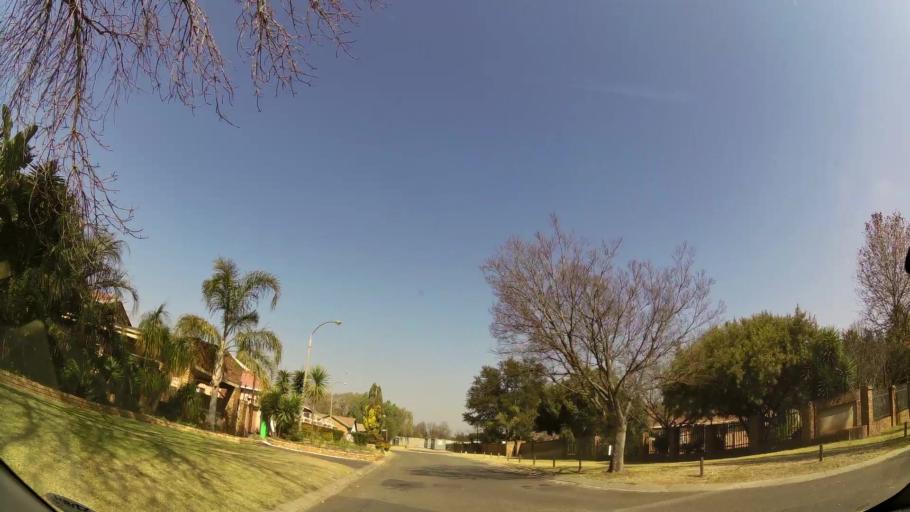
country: ZA
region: Gauteng
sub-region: Ekurhuleni Metropolitan Municipality
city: Boksburg
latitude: -26.1715
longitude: 28.2653
